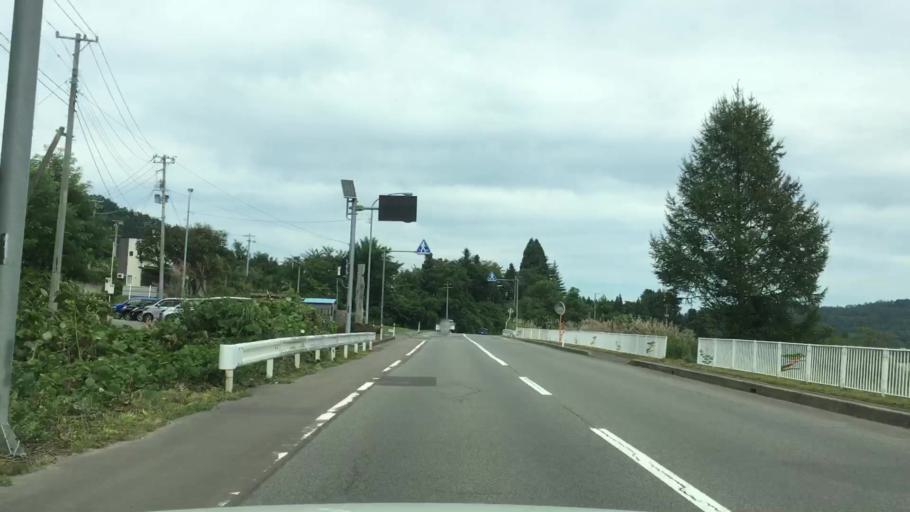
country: JP
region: Aomori
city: Shimokizukuri
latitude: 40.7500
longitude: 140.2294
